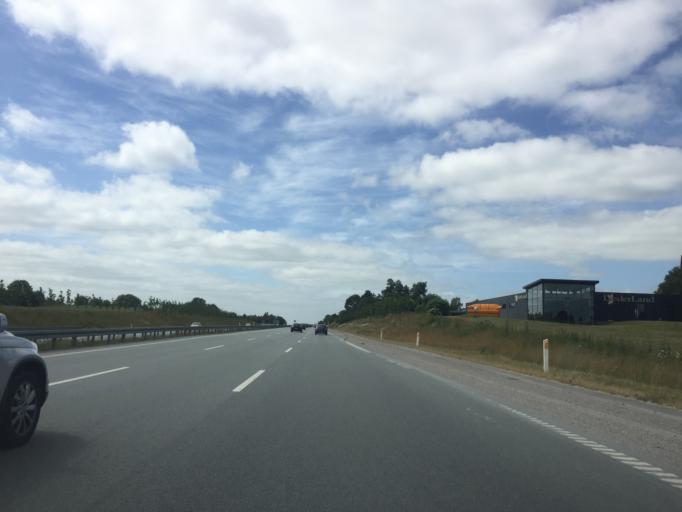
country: DK
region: Zealand
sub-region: Roskilde Kommune
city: Vindinge
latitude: 55.6415
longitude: 12.1265
